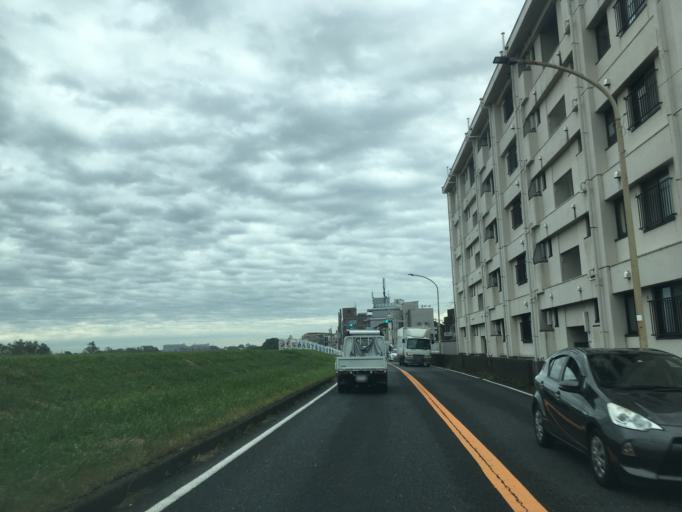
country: JP
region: Tokyo
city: Chofugaoka
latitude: 35.6337
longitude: 139.5498
